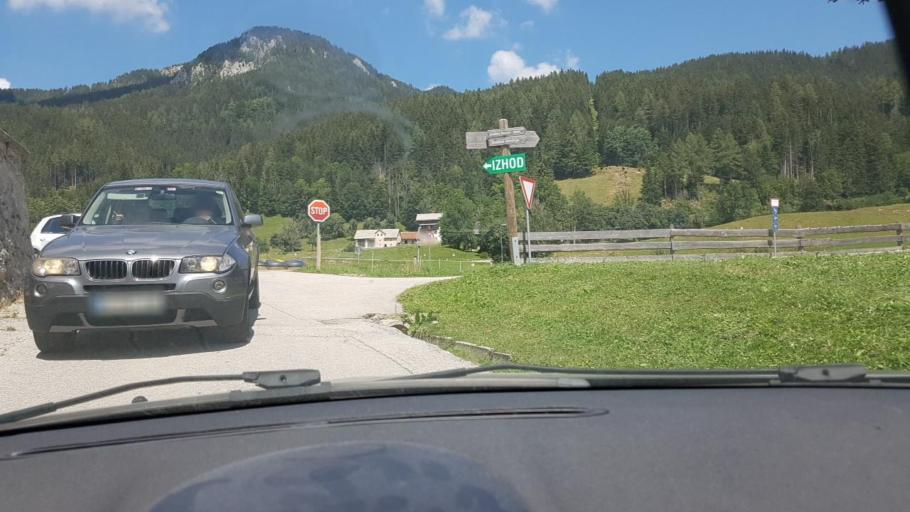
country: SI
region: Jezersko
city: Zgornje Jezersko
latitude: 46.4078
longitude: 14.5176
